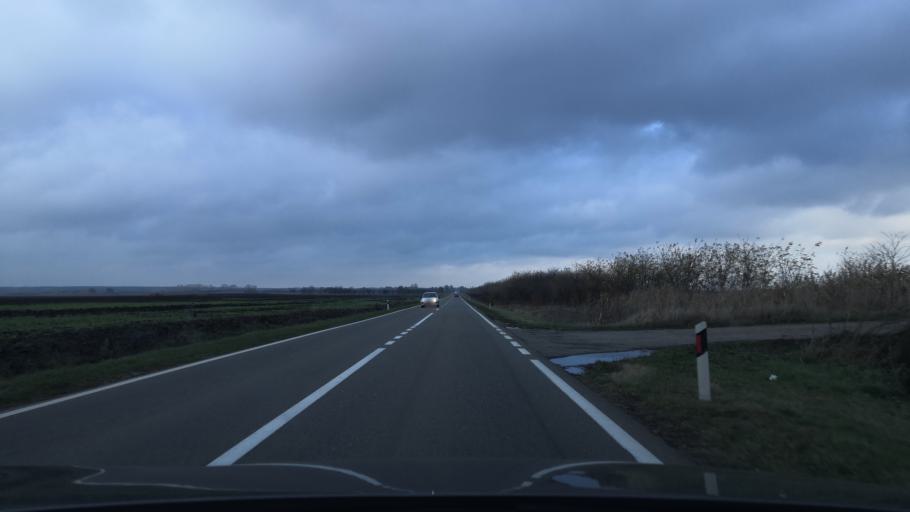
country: RS
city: Sanad
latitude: 46.0066
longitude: 20.1005
